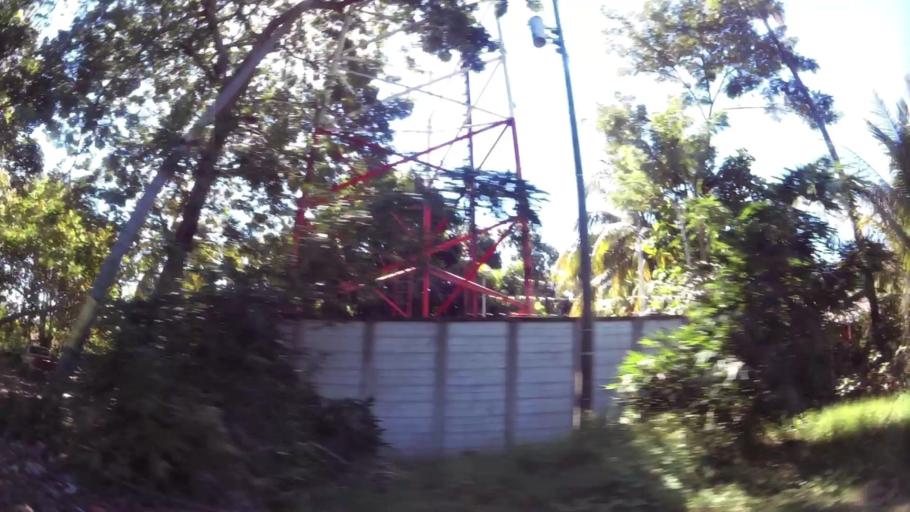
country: GT
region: Escuintla
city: Iztapa
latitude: 13.9239
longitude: -90.5907
